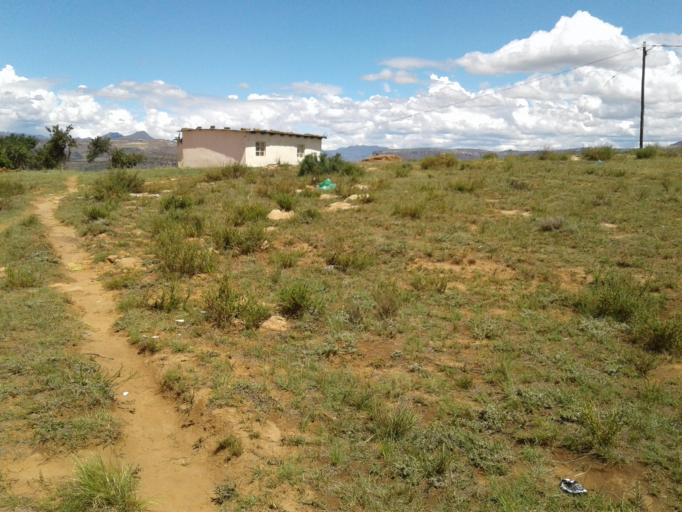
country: LS
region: Quthing
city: Quthing
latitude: -30.3771
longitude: 27.5577
